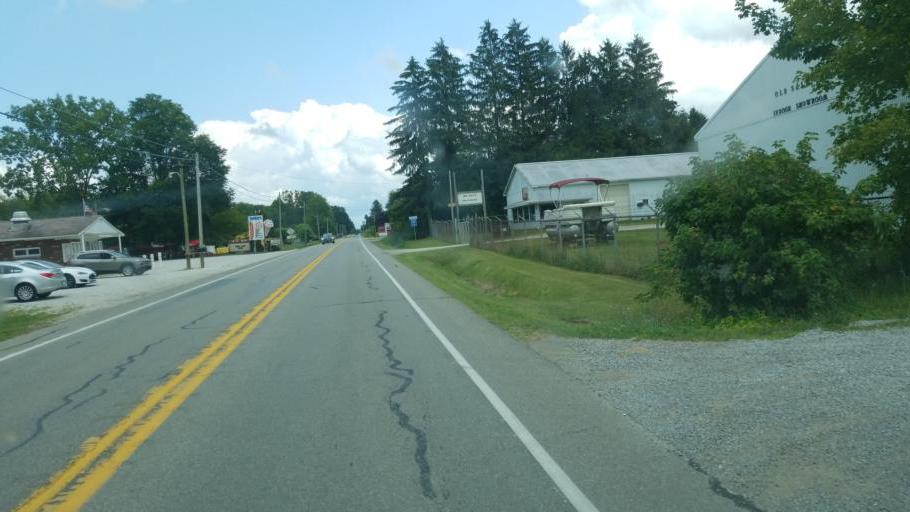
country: US
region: Pennsylvania
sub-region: Crawford County
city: Pymatuning Central
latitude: 41.6065
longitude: -80.4984
